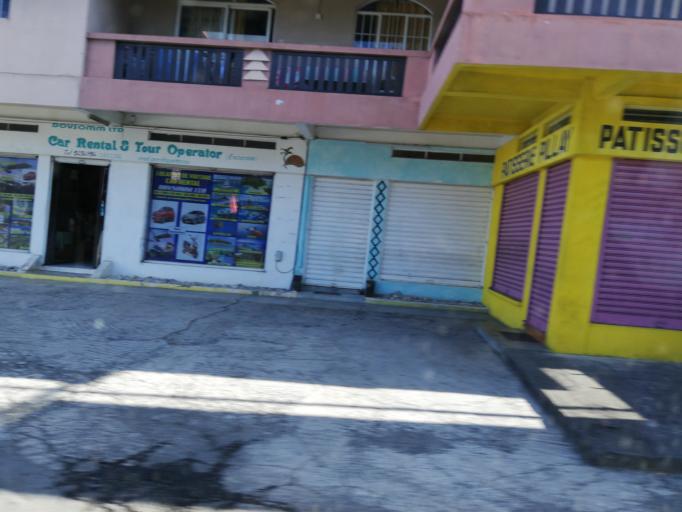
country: MU
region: Riviere du Rempart
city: Grand Baie
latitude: -20.0110
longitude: 57.5642
